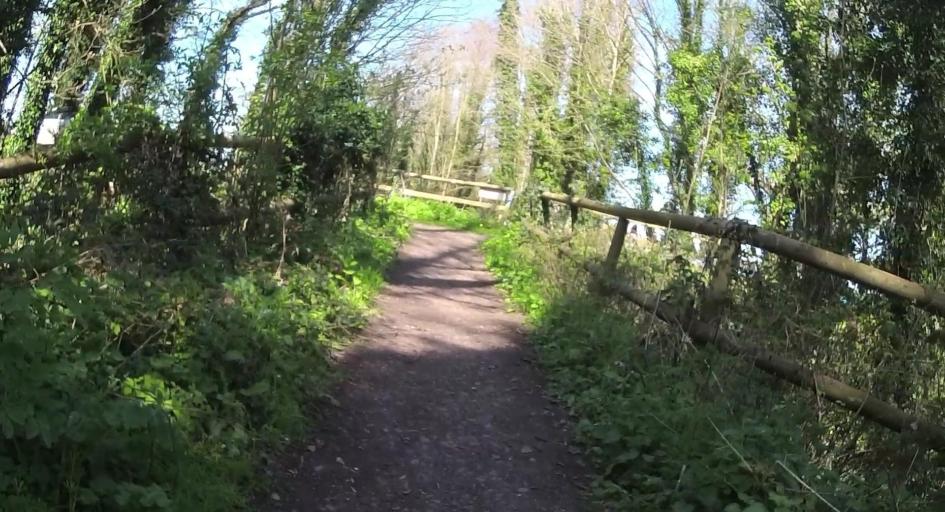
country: GB
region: England
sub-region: Hampshire
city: Romsey
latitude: 51.0727
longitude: -1.5095
